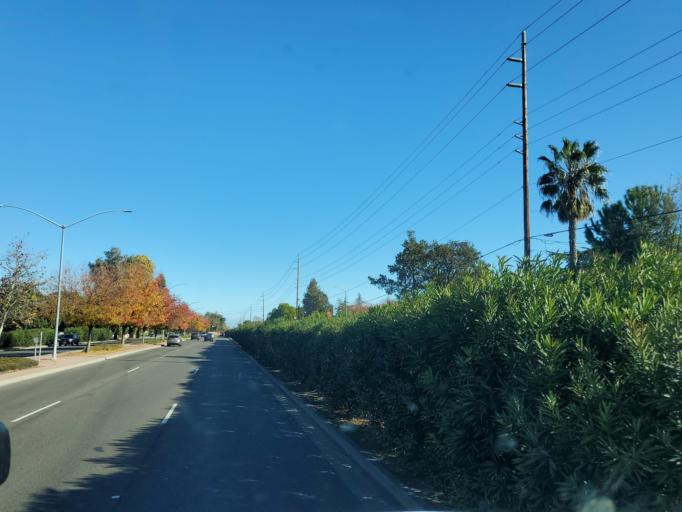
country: US
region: California
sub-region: San Joaquin County
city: Lincoln Village
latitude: 38.0212
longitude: -121.3415
